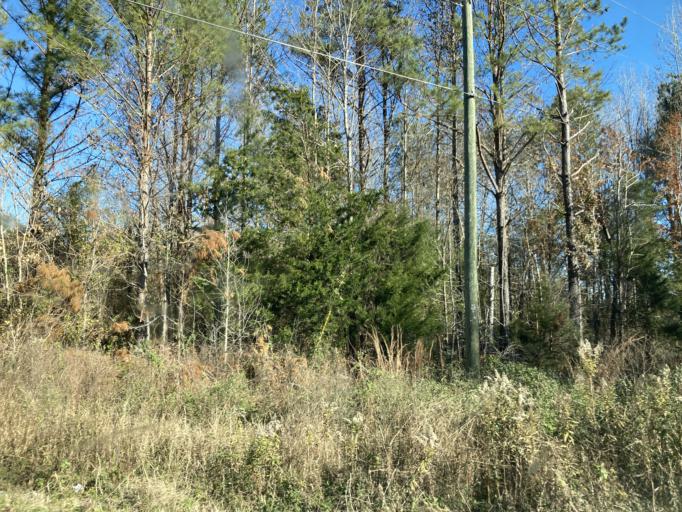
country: US
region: Mississippi
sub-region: Holmes County
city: Pickens
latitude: 32.8562
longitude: -90.0167
